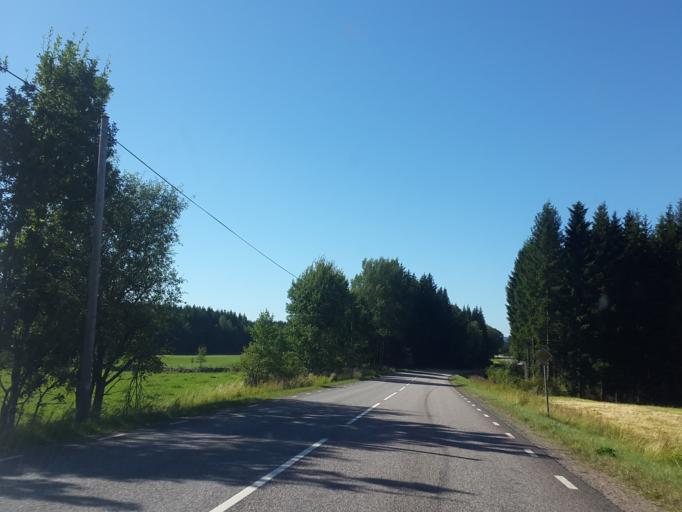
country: SE
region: Vaestra Goetaland
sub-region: Boras Kommun
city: Dalsjofors
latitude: 57.8625
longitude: 13.0213
